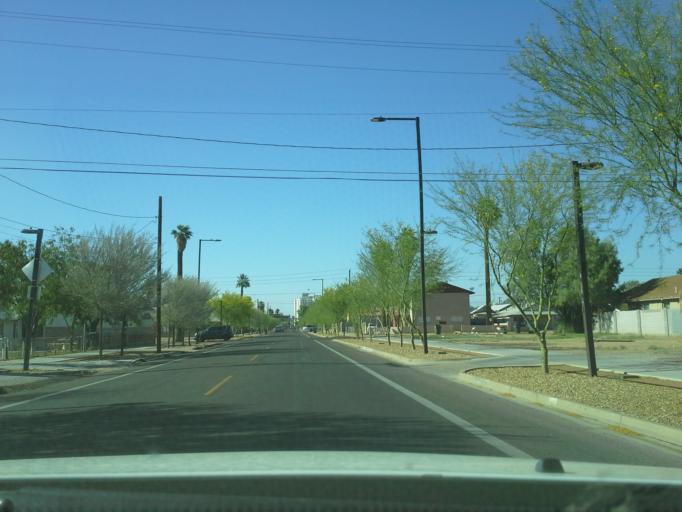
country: US
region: Arizona
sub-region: Maricopa County
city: Phoenix
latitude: 33.4551
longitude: -112.0589
